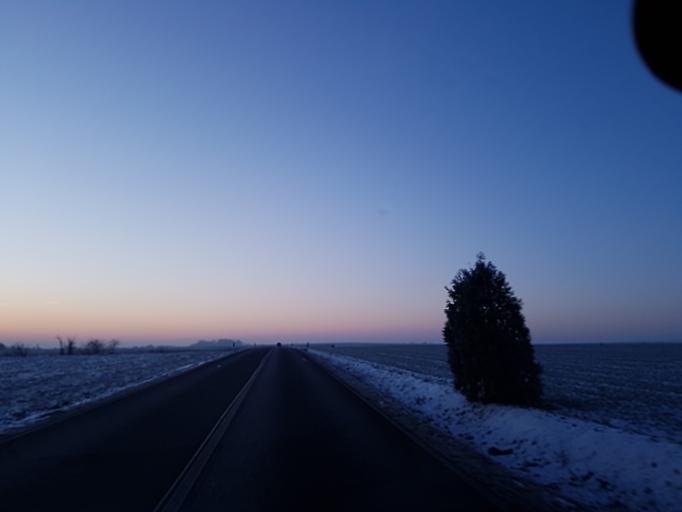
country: DE
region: Saxony
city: Strehla
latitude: 51.3807
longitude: 13.2016
